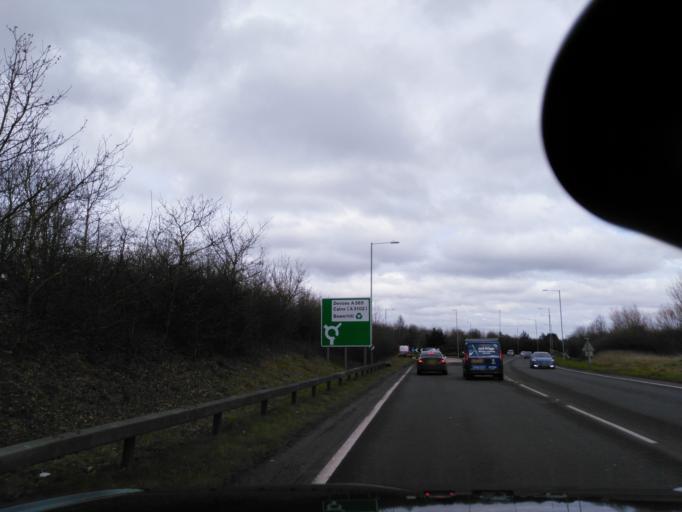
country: GB
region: England
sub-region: Wiltshire
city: Melksham
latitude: 51.3621
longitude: -2.1376
